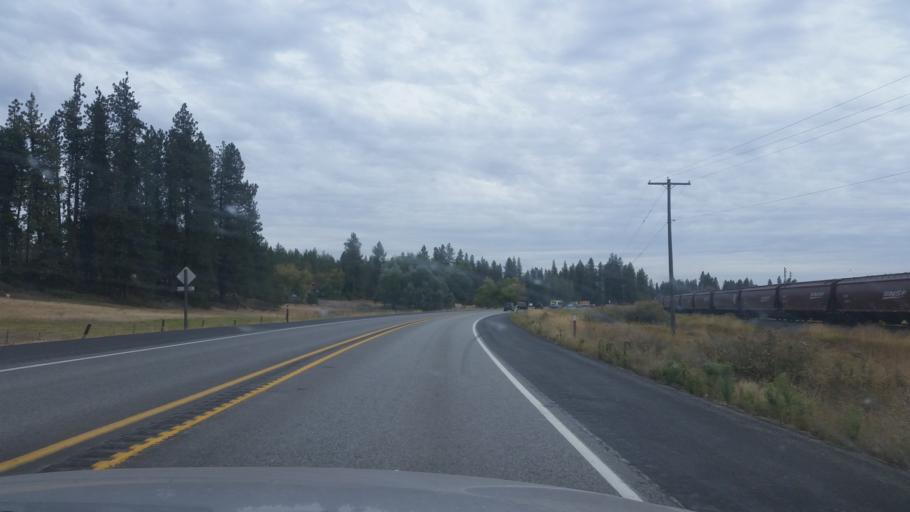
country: US
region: Washington
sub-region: Spokane County
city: Cheney
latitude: 47.5281
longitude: -117.5680
